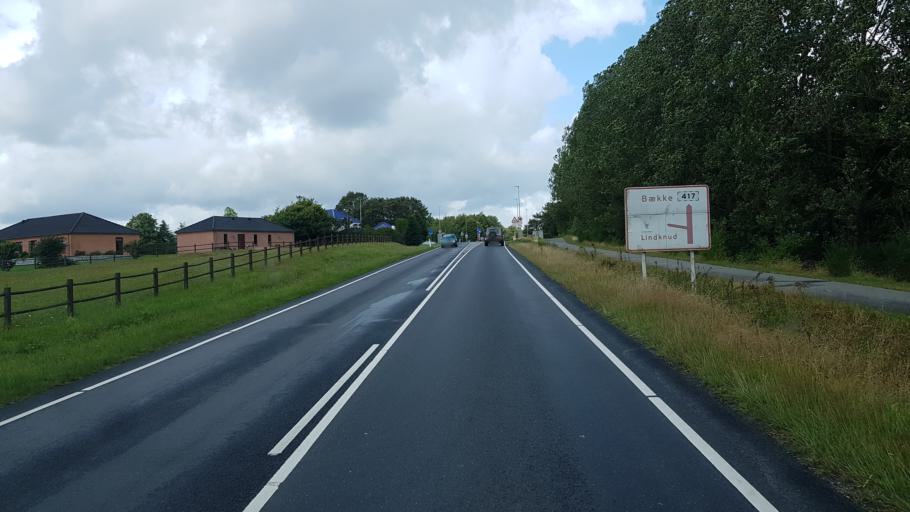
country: DK
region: South Denmark
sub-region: Vejen Kommune
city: Vejen
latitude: 55.5214
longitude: 9.1187
